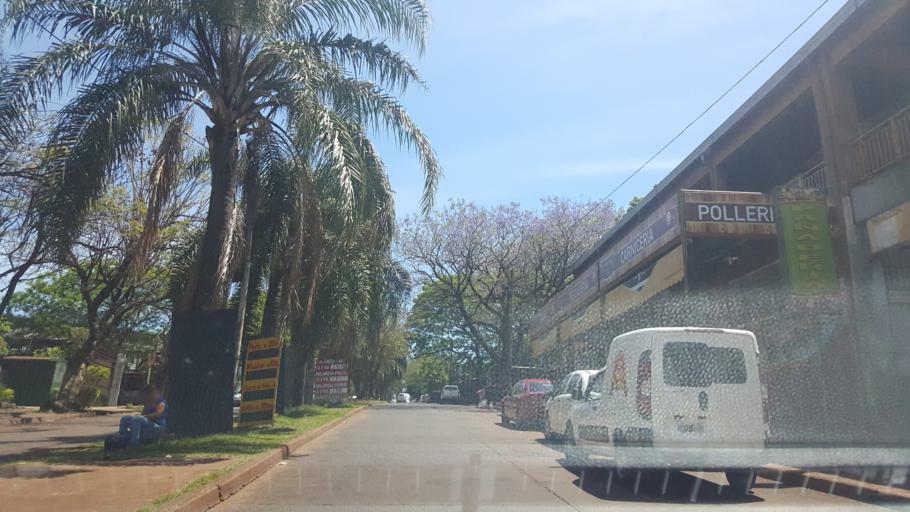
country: AR
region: Misiones
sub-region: Departamento de Capital
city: Posadas
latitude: -27.3970
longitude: -55.9070
